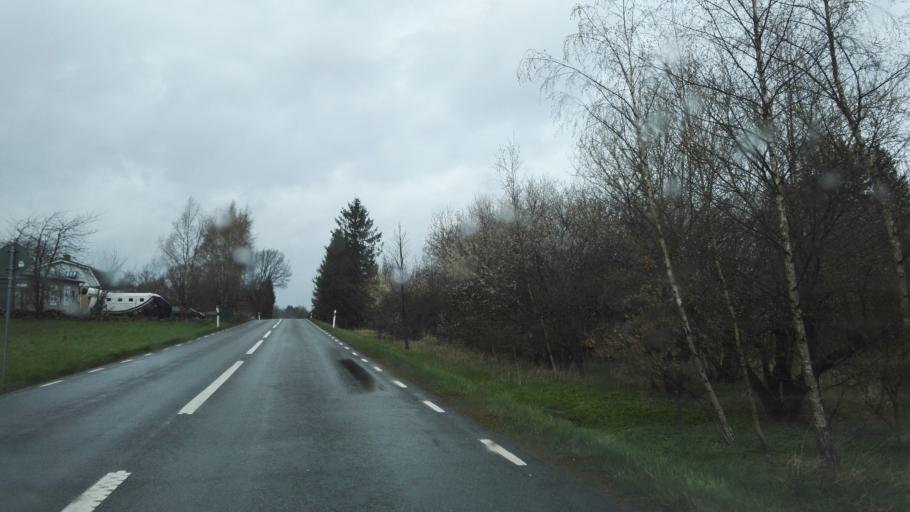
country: SE
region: Skane
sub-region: Simrishamns Kommun
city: Kivik
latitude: 55.6671
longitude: 14.2225
